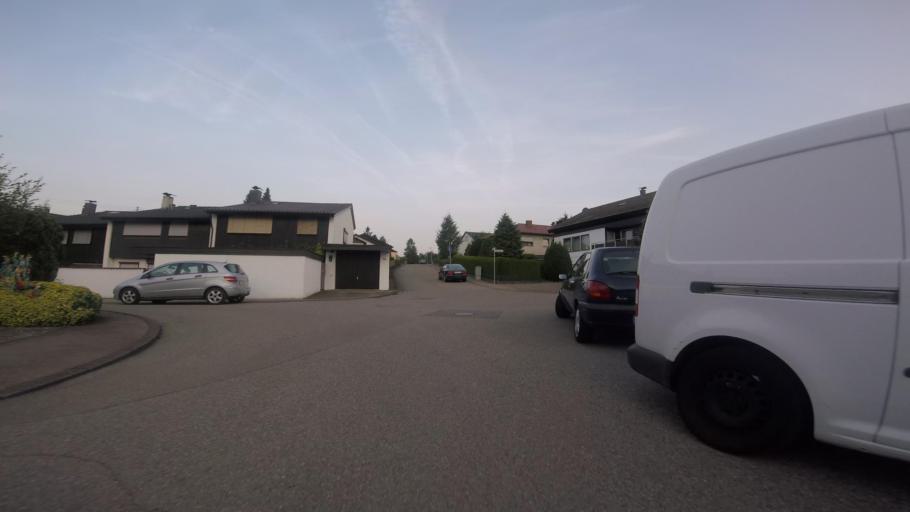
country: DE
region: Baden-Wuerttemberg
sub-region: Regierungsbezirk Stuttgart
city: Aspach
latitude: 48.9697
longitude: 9.3944
